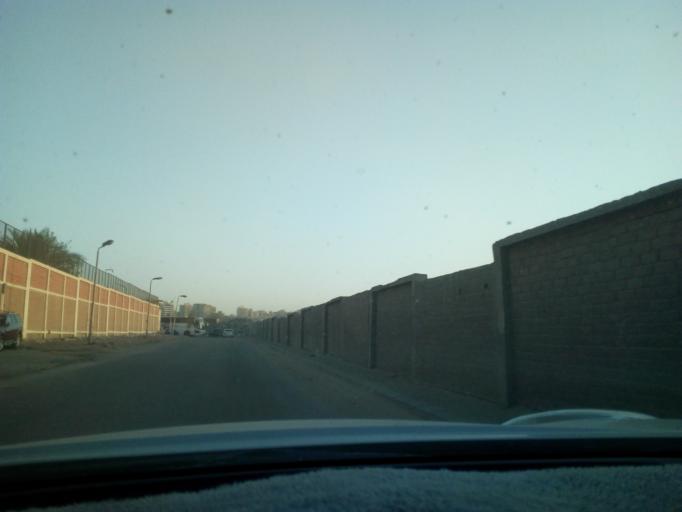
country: EG
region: Muhafazat al Qalyubiyah
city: Al Khankah
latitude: 30.1251
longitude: 31.3559
